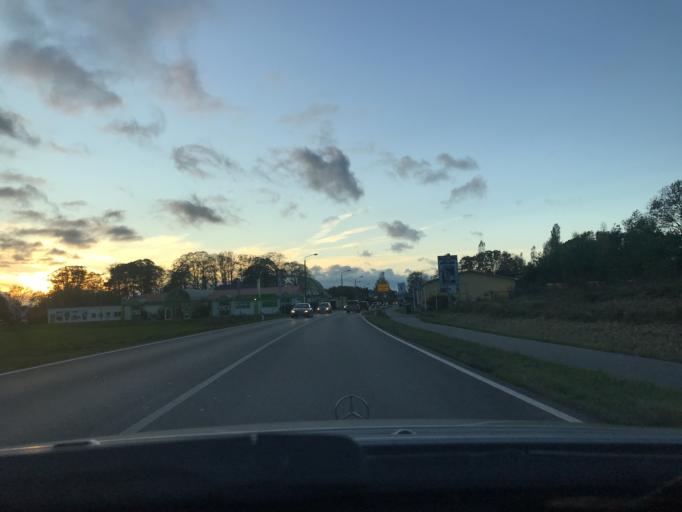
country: DE
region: Mecklenburg-Vorpommern
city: Ostseebad Zinnowitz
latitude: 54.0669
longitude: 13.9228
